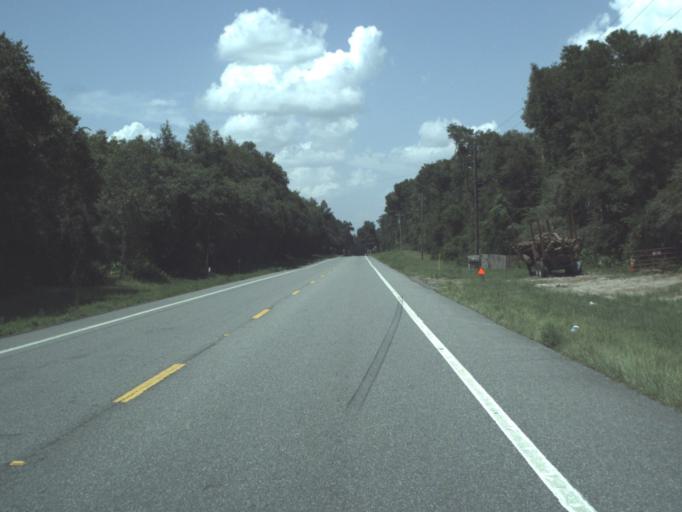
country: US
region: Florida
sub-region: Hernando County
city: Ridge Manor
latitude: 28.5658
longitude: -82.1564
